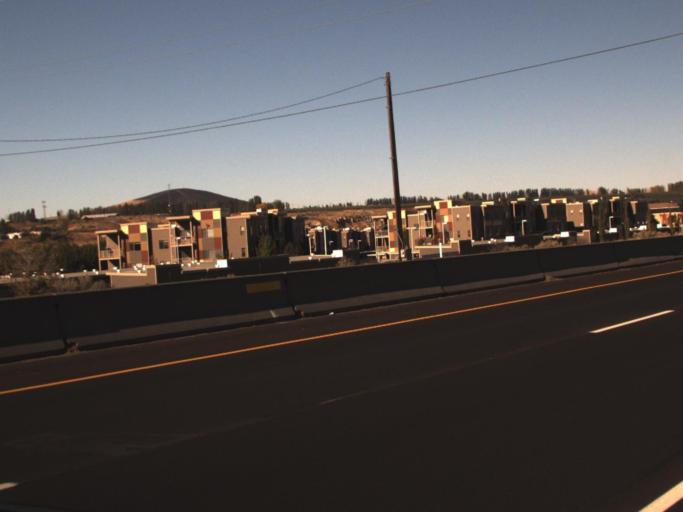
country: US
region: Washington
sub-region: Benton County
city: Richland
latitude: 46.2647
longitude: -119.2966
